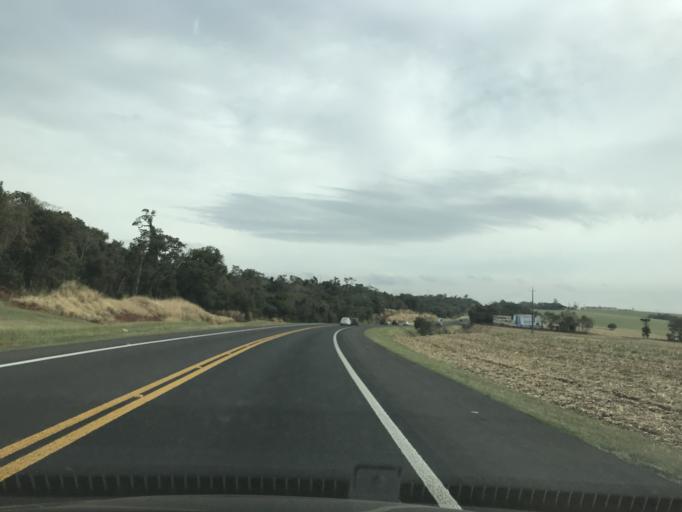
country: BR
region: Parana
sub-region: Matelandia
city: Matelandia
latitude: -25.1174
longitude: -53.7972
